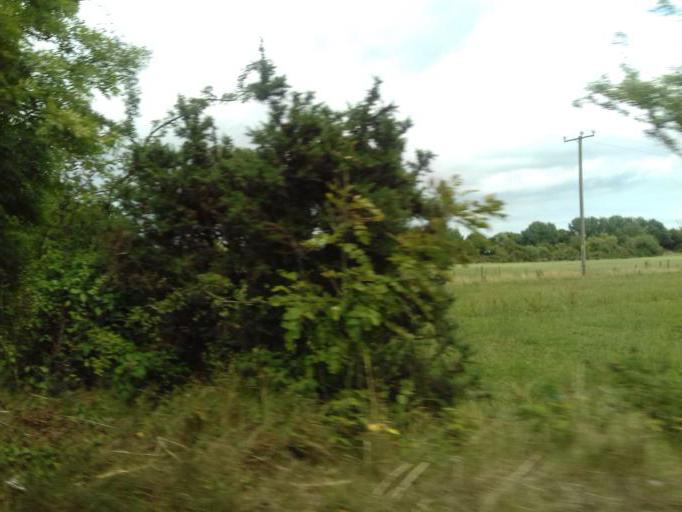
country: IE
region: Leinster
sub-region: Loch Garman
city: Ballinroad
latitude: 52.4552
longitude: -6.4005
